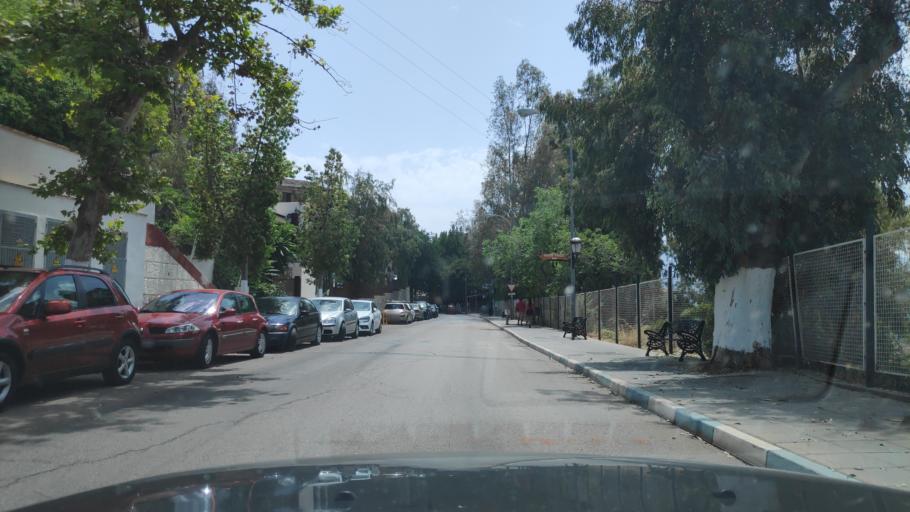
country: ES
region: Andalusia
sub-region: Provincia de Granada
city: Lanjaron
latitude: 36.9197
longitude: -3.4905
